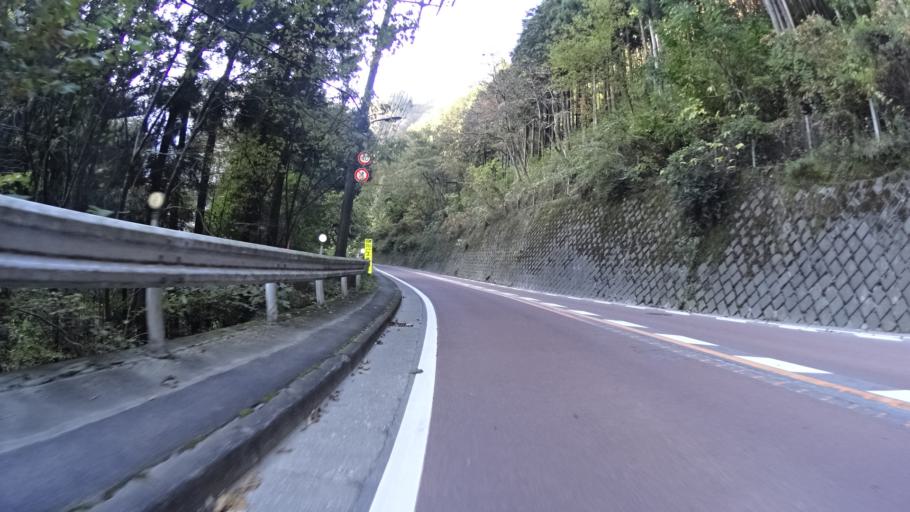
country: JP
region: Tokyo
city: Itsukaichi
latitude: 35.7246
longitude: 139.1454
